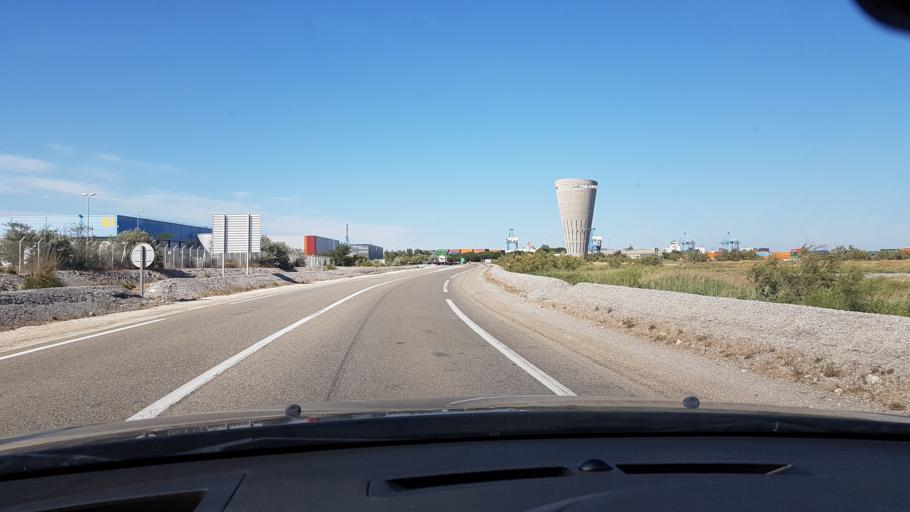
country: FR
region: Provence-Alpes-Cote d'Azur
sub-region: Departement des Bouches-du-Rhone
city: Port-Saint-Louis-du-Rhone
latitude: 43.4022
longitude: 4.8272
